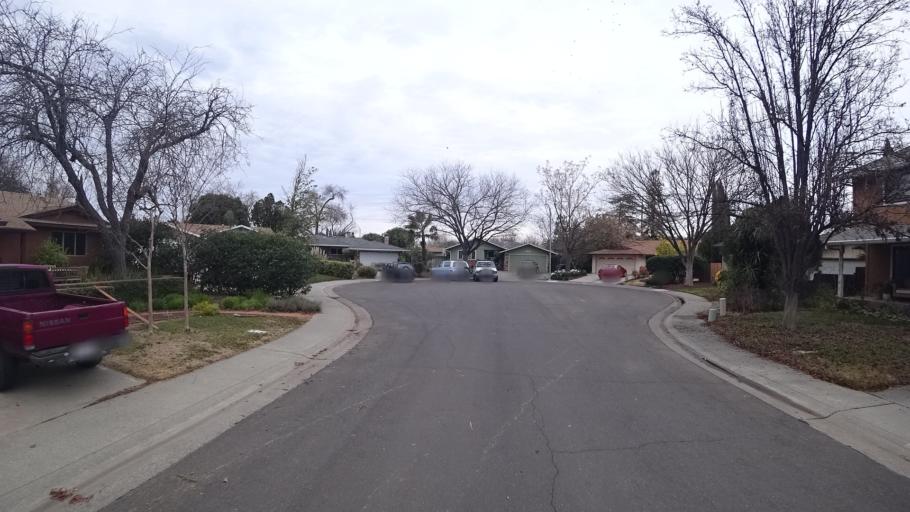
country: US
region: California
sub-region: Yolo County
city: Davis
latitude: 38.5626
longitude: -121.7172
